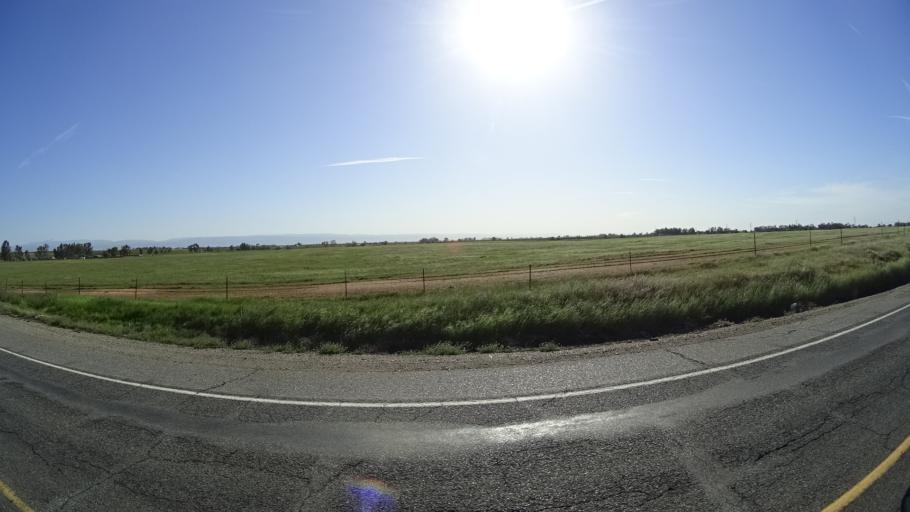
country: US
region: California
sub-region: Glenn County
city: Orland
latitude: 39.8085
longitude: -122.1979
